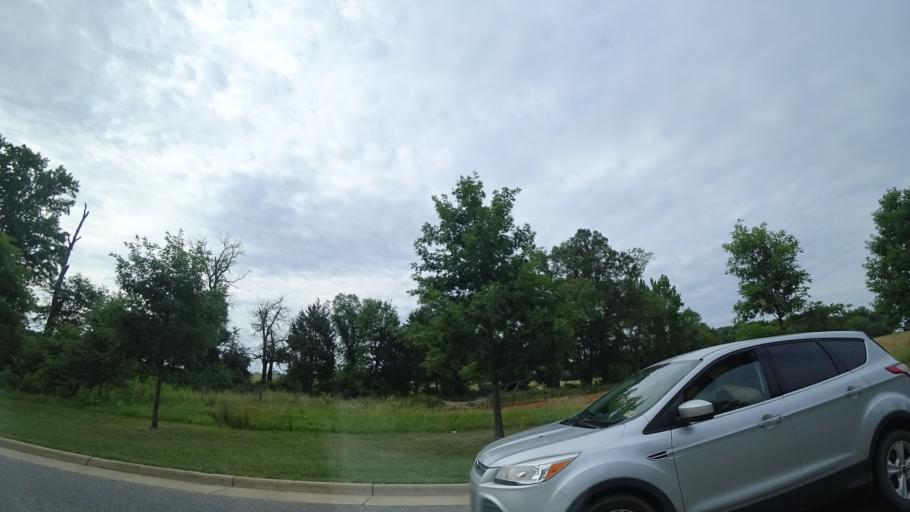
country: US
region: Virginia
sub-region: Spotsylvania County
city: Spotsylvania
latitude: 38.2073
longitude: -77.5857
